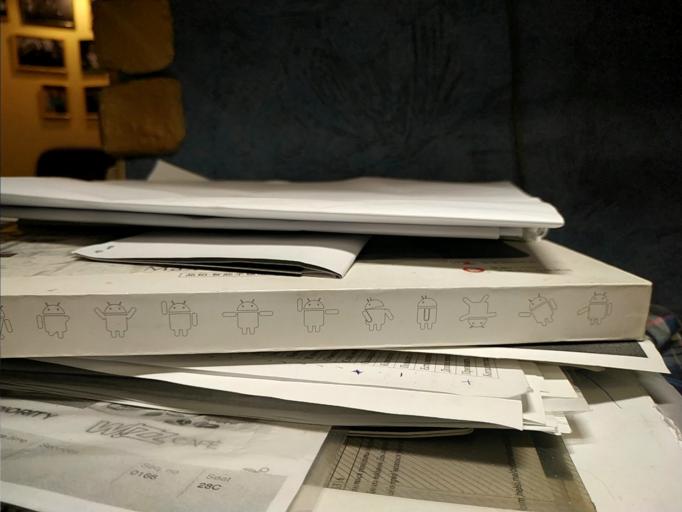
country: RU
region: Tverskaya
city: Zubtsov
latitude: 56.0792
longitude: 34.8080
